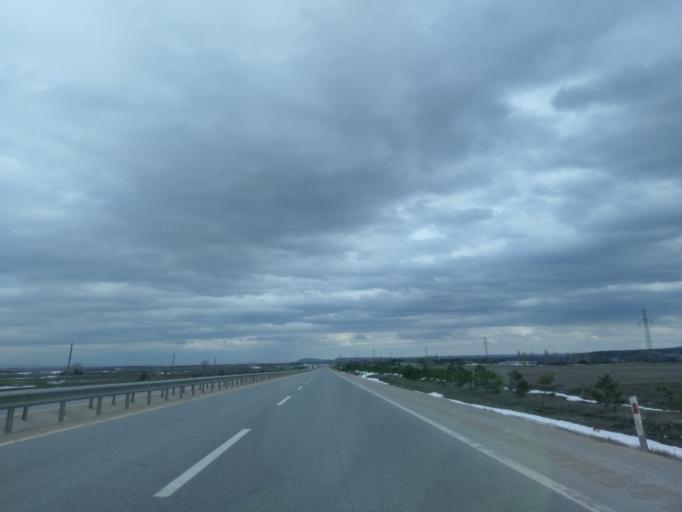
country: TR
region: Eskisehir
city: Inonu
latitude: 39.7245
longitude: 30.2820
